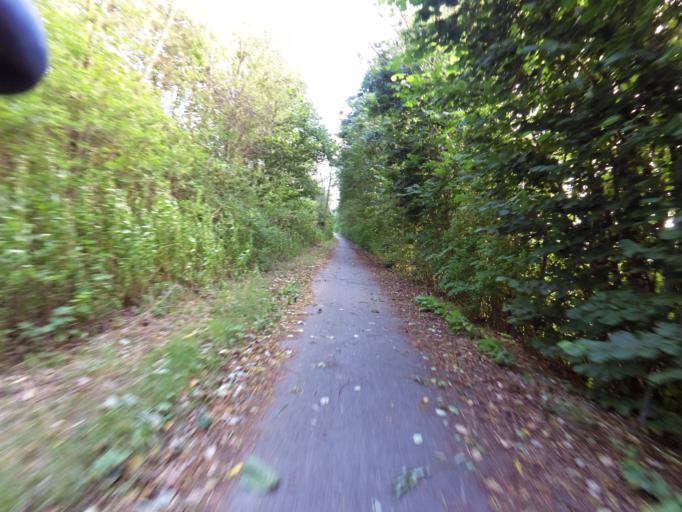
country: DE
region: Bavaria
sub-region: Upper Bavaria
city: Hallbergmoos
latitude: 48.3525
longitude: 11.7381
